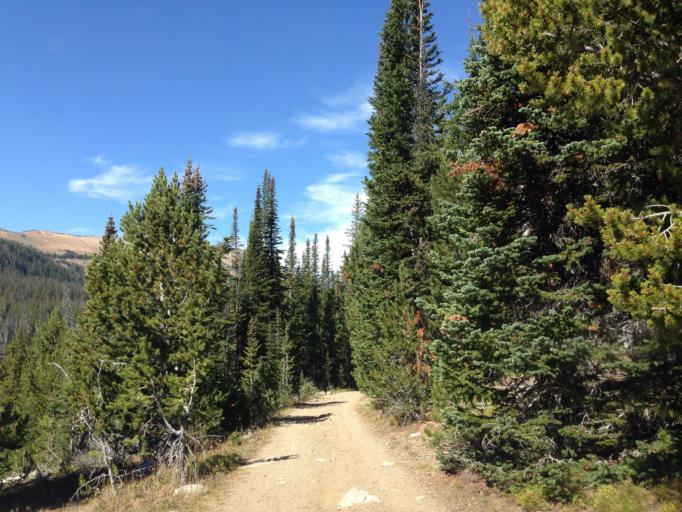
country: US
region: Montana
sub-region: Stillwater County
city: Absarokee
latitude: 45.0505
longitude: -109.9102
